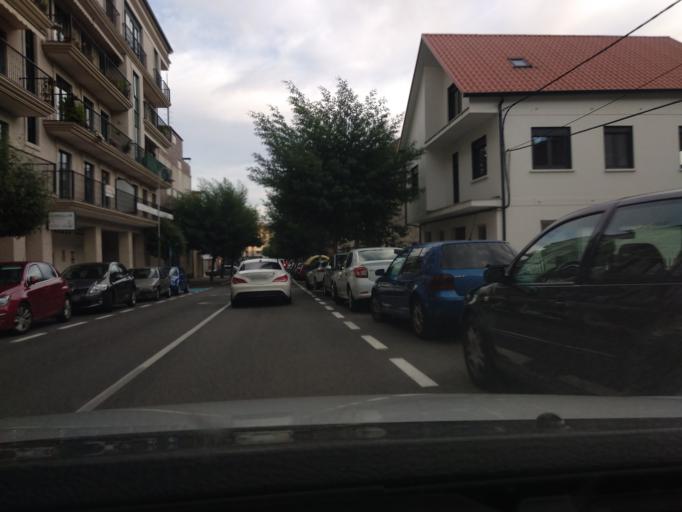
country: ES
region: Galicia
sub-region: Provincia de Pontevedra
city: Moana
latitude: 42.2883
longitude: -8.7351
